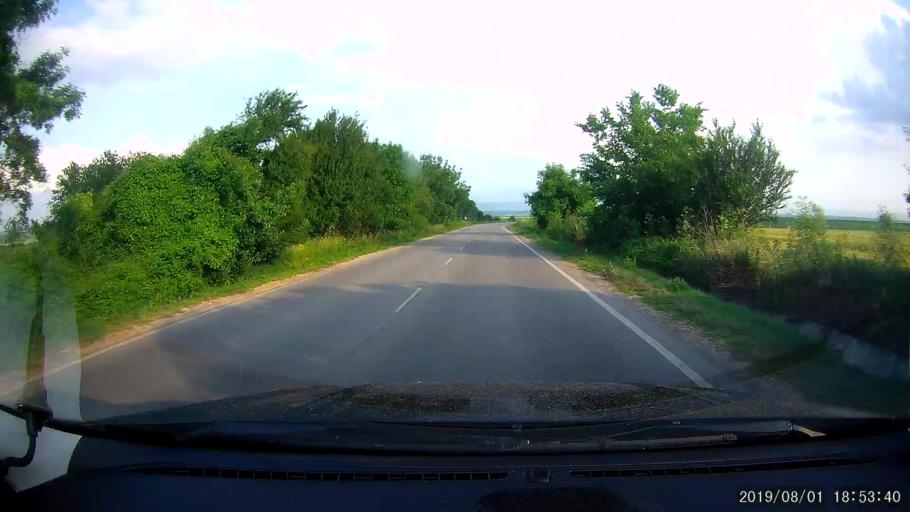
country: BG
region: Shumen
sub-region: Obshtina Shumen
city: Shumen
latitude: 43.2172
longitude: 26.9964
